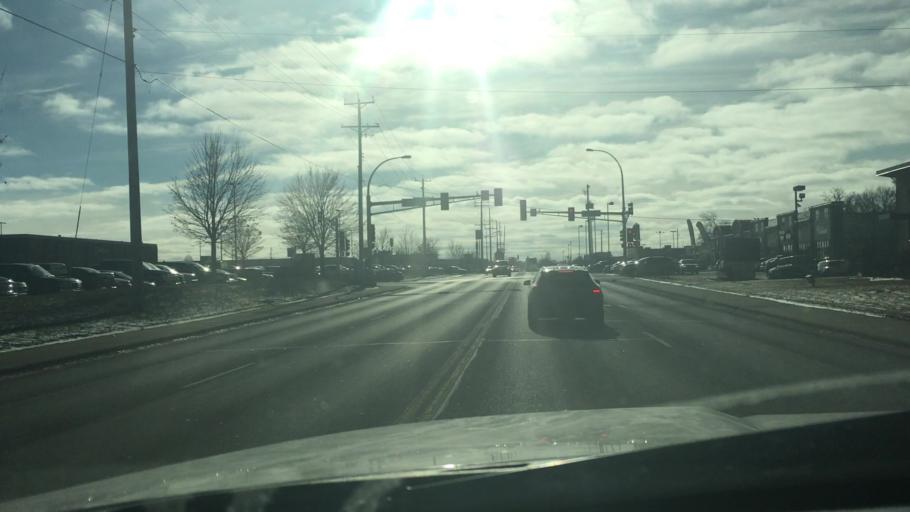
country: US
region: Minnesota
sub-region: Stearns County
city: Waite Park
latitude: 45.5568
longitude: -94.2138
